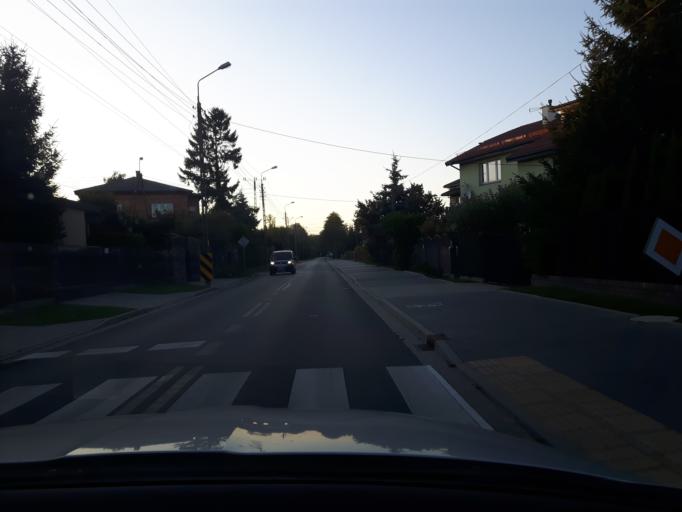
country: PL
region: Masovian Voivodeship
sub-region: Powiat wolominski
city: Kobylka
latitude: 52.3324
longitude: 21.1902
